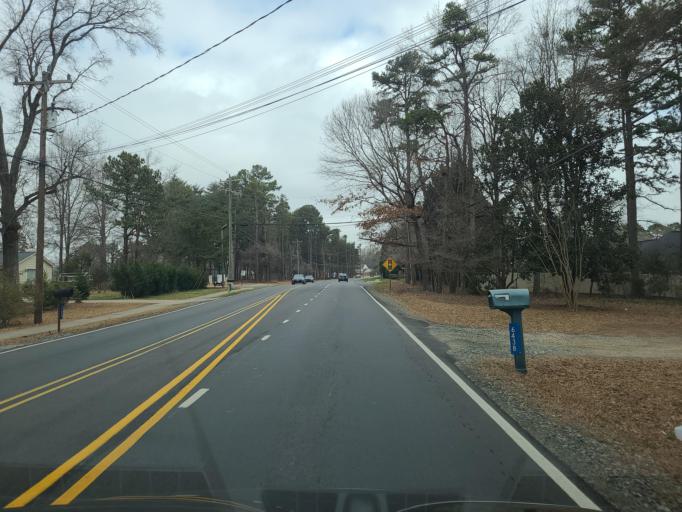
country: US
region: North Carolina
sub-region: Mecklenburg County
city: Mint Hill
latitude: 35.1921
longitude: -80.6864
